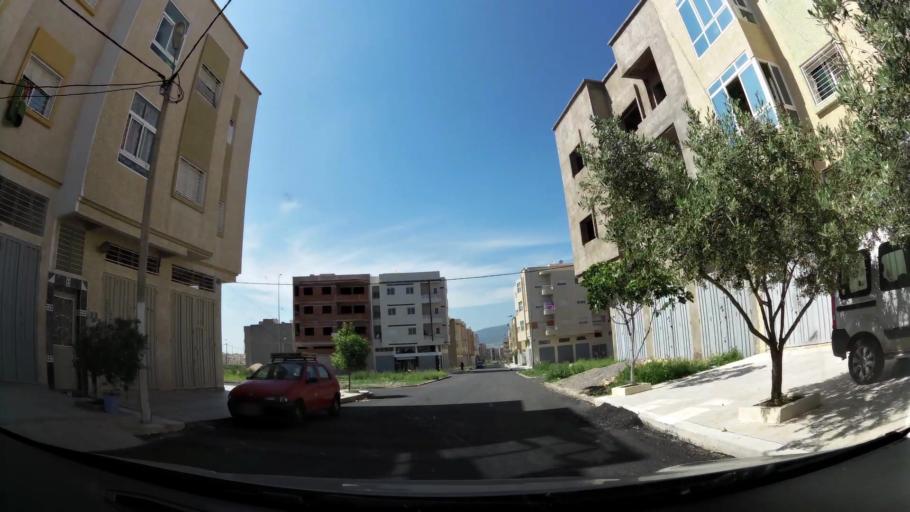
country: MA
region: Fes-Boulemane
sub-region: Fes
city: Fes
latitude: 34.0089
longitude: -5.0349
